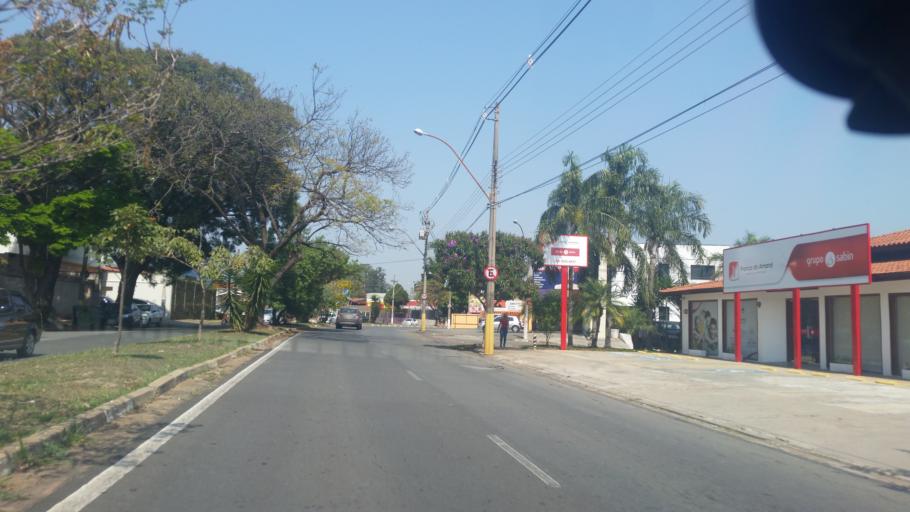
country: BR
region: Sao Paulo
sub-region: Campinas
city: Campinas
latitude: -22.8330
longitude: -47.0773
